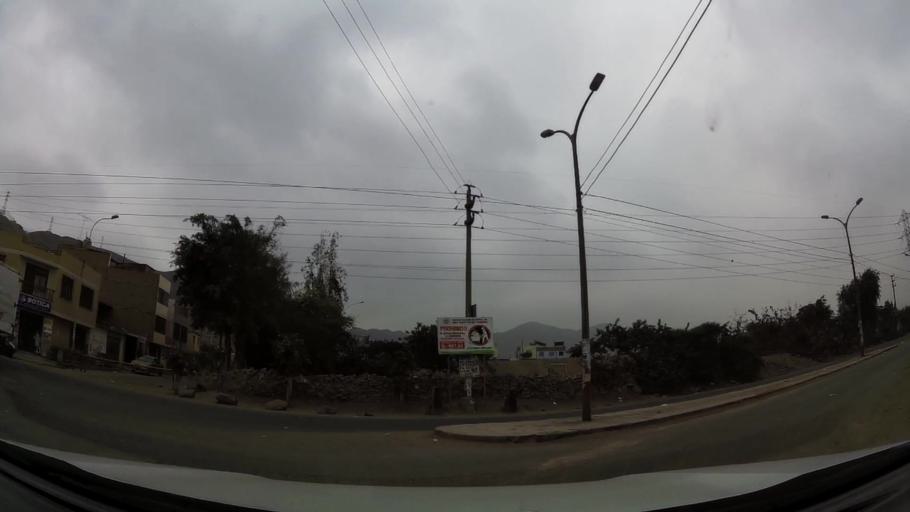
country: PE
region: Lima
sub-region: Lima
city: Independencia
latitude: -11.9455
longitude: -77.0915
